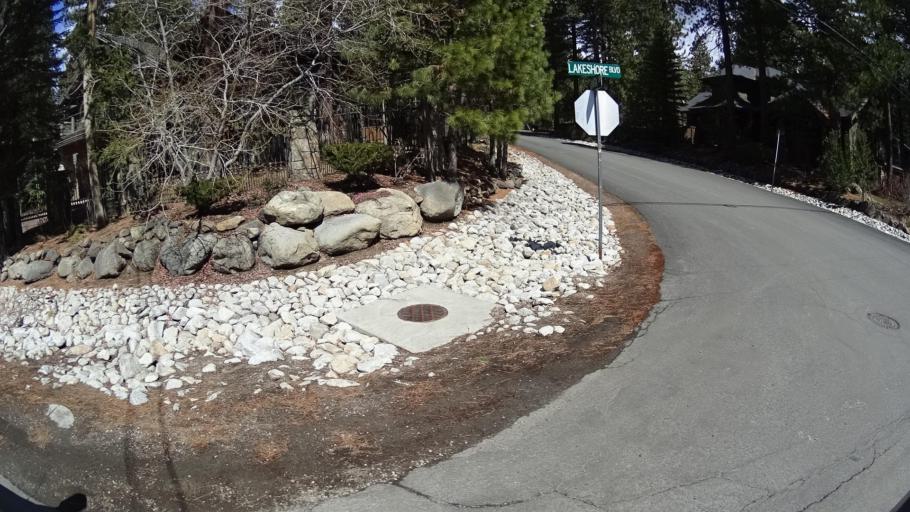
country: US
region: Nevada
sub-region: Washoe County
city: Incline Village
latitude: 39.2421
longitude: -119.9532
